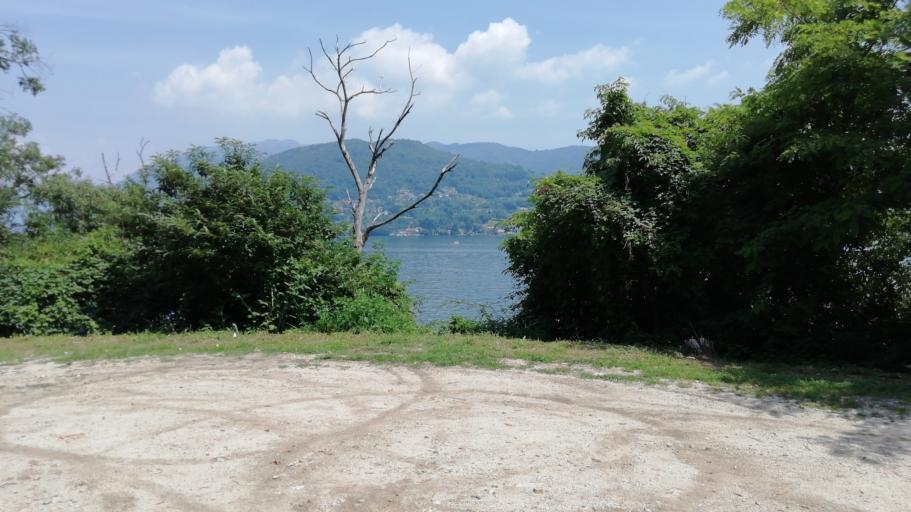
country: IT
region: Piedmont
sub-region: Provincia di Novara
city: Pella
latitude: 45.8138
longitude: 8.3861
